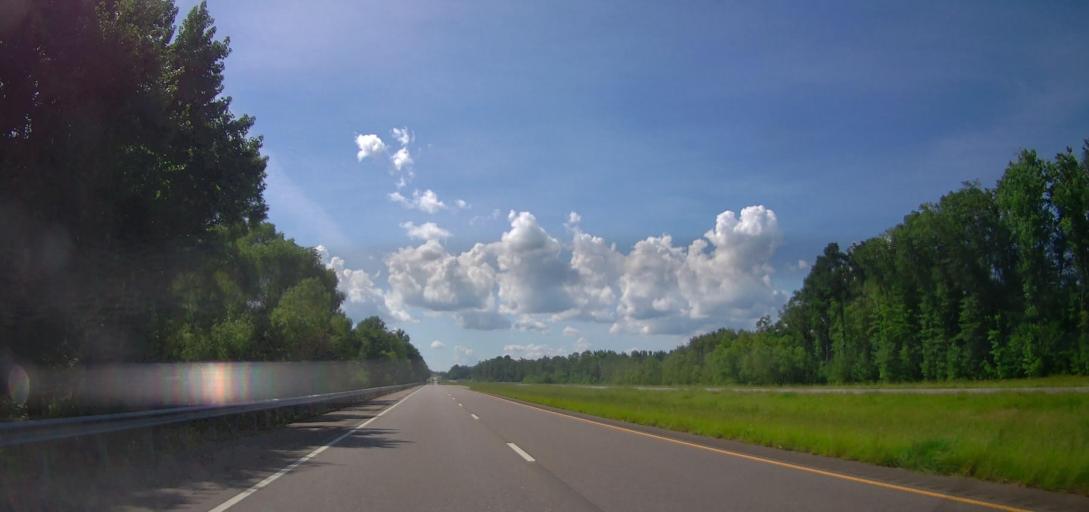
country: US
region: Alabama
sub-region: Pickens County
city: Gordo
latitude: 33.3440
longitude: -87.9457
